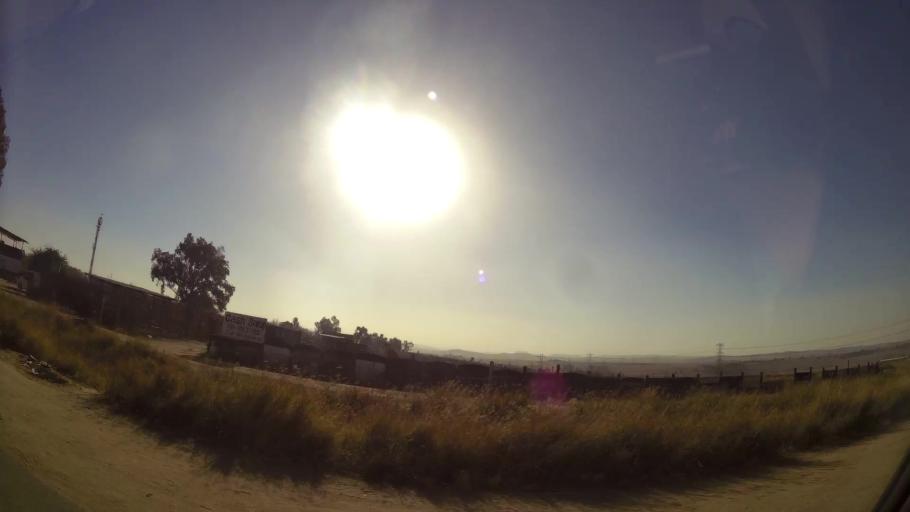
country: ZA
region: Gauteng
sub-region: City of Johannesburg Metropolitan Municipality
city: Diepsloot
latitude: -25.9354
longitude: 27.9915
